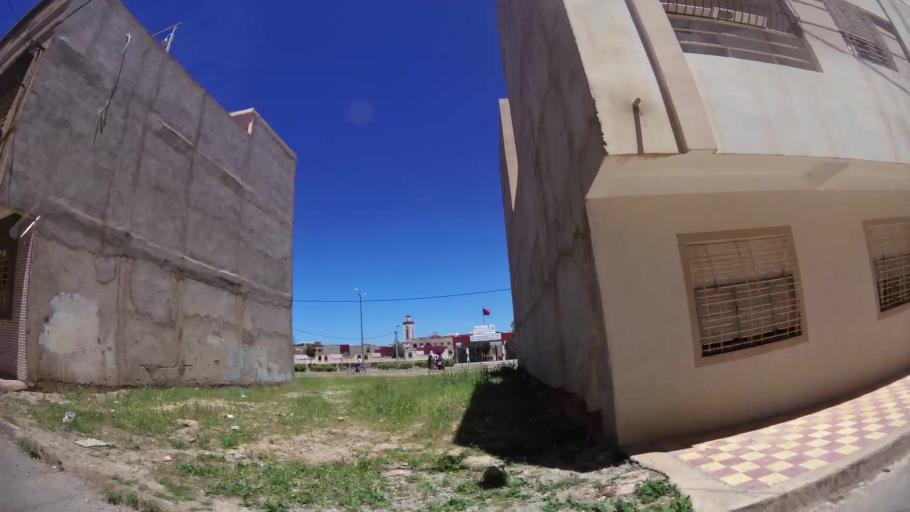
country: MA
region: Oriental
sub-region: Oujda-Angad
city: Oujda
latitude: 34.6818
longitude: -1.8720
